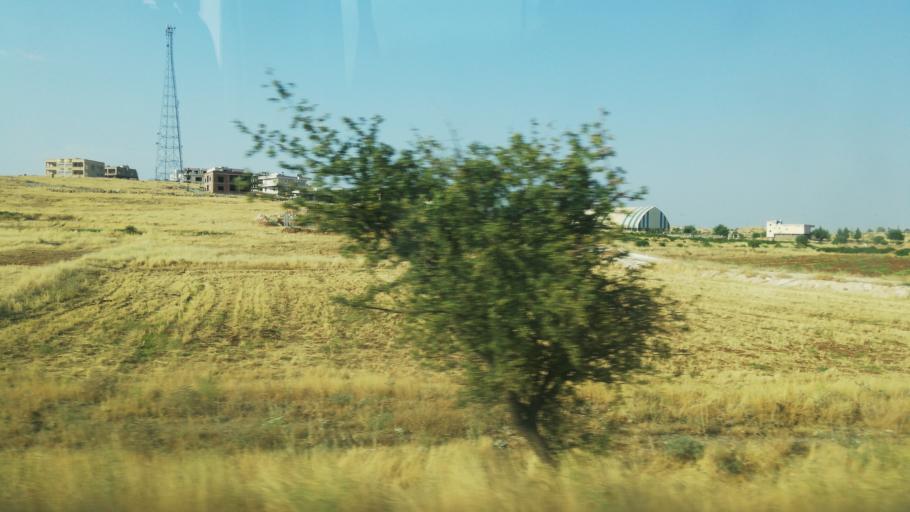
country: TR
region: Mardin
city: Acirli
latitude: 37.4409
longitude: 41.2922
